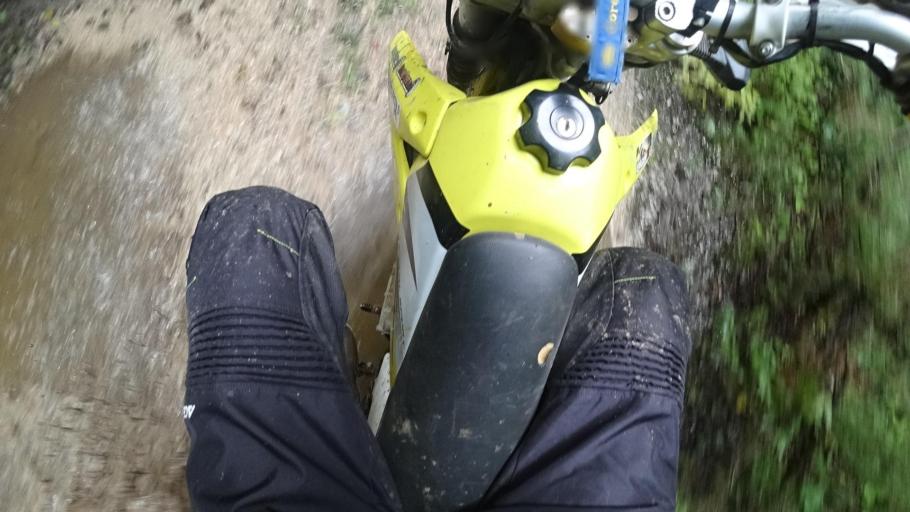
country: BA
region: Republika Srpska
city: Bronzani Majdan
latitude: 44.6337
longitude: 17.0233
